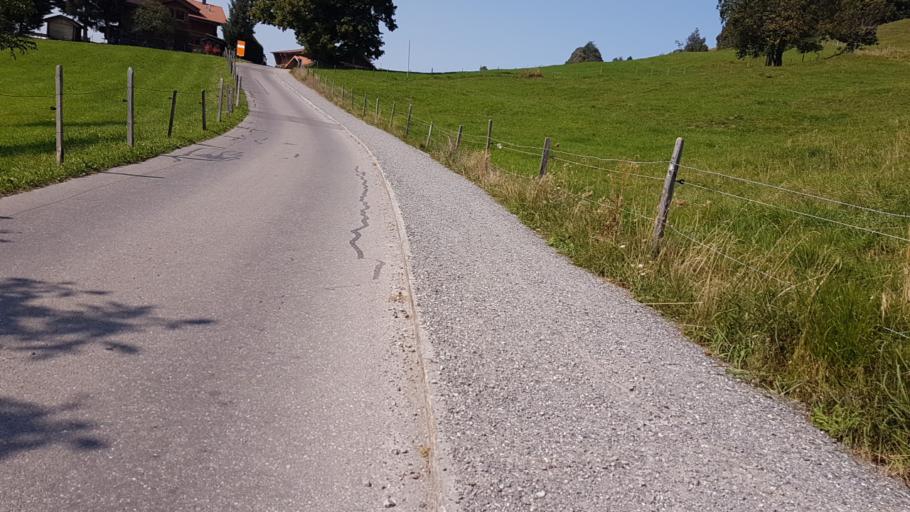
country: CH
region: Bern
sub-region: Frutigen-Niedersimmental District
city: Aeschi
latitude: 46.6387
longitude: 7.7336
